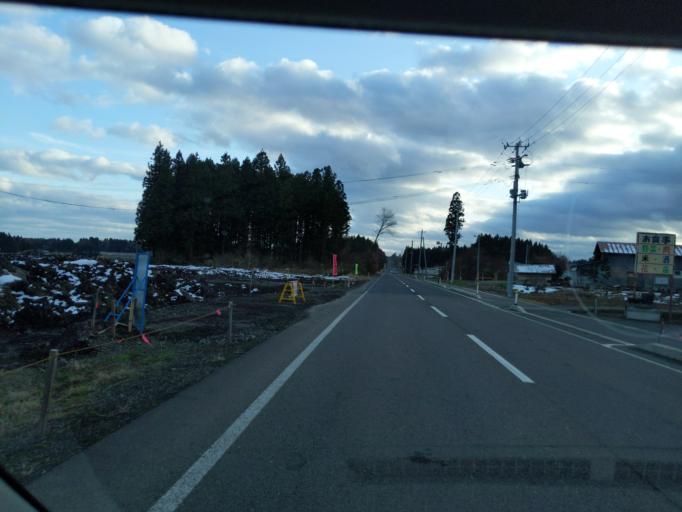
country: JP
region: Iwate
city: Mizusawa
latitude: 39.1017
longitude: 141.0514
